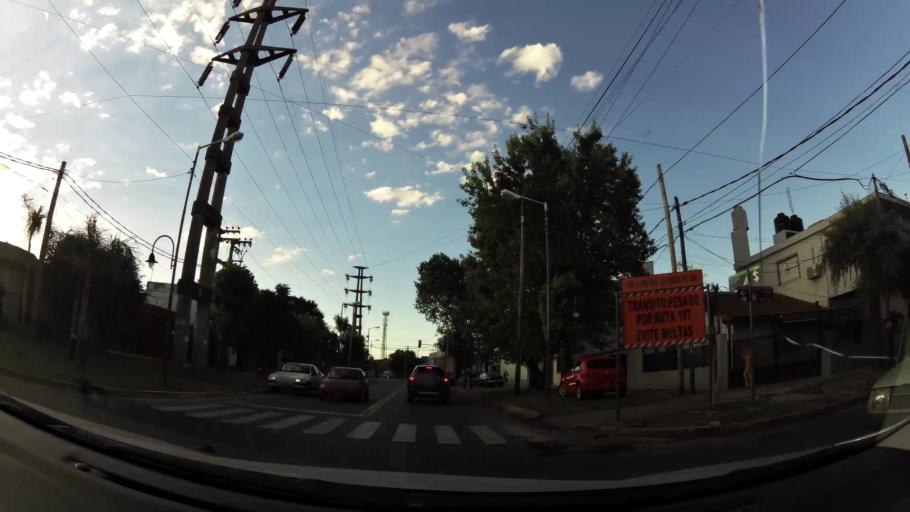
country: AR
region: Buenos Aires
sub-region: Partido de Tigre
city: Tigre
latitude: -34.4510
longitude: -58.5693
